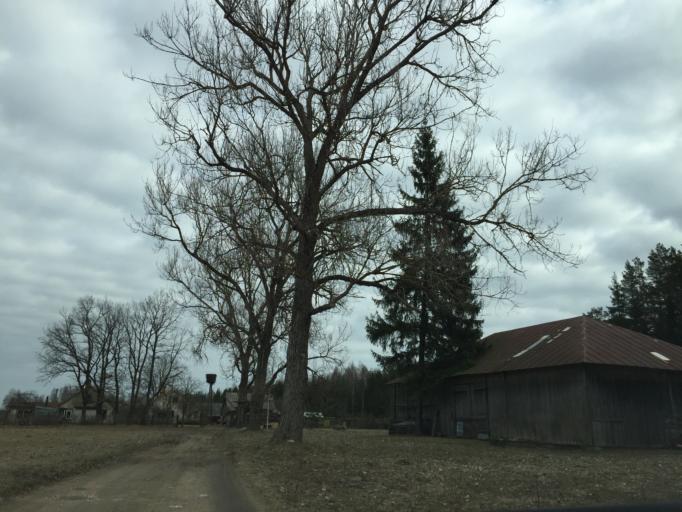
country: LV
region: Incukalns
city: Vangazi
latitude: 57.1042
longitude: 24.5482
